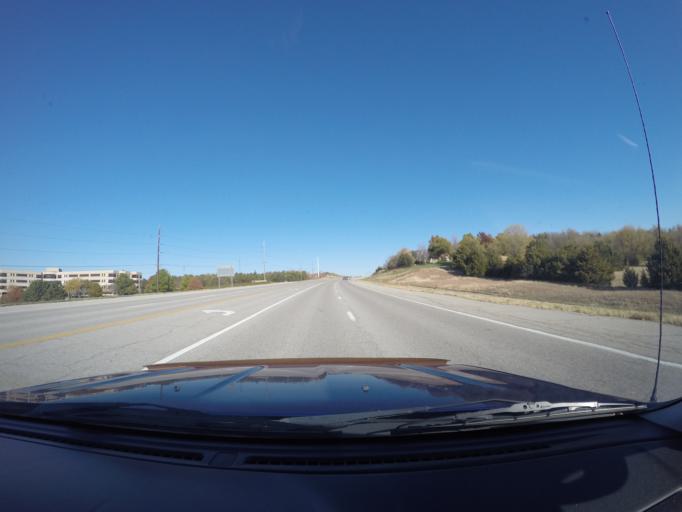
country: US
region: Kansas
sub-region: Riley County
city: Manhattan
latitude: 39.2158
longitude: -96.6181
